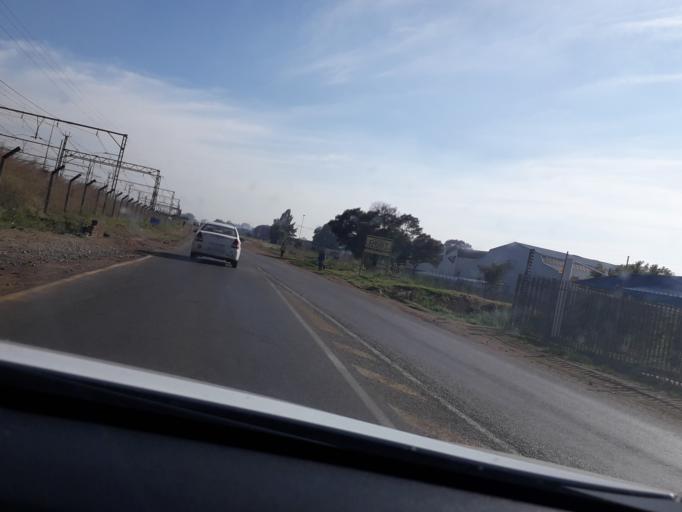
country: ZA
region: Gauteng
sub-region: Ekurhuleni Metropolitan Municipality
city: Boksburg
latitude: -26.1558
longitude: 28.2127
